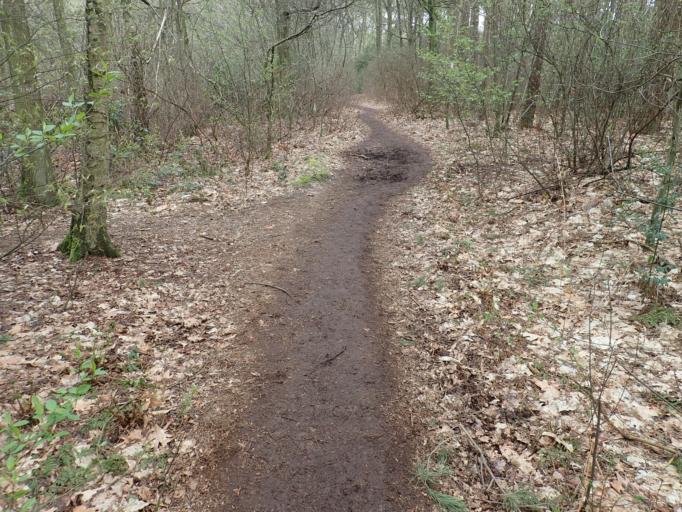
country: BE
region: Flanders
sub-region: Provincie Antwerpen
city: Vorselaar
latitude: 51.2096
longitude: 4.7735
